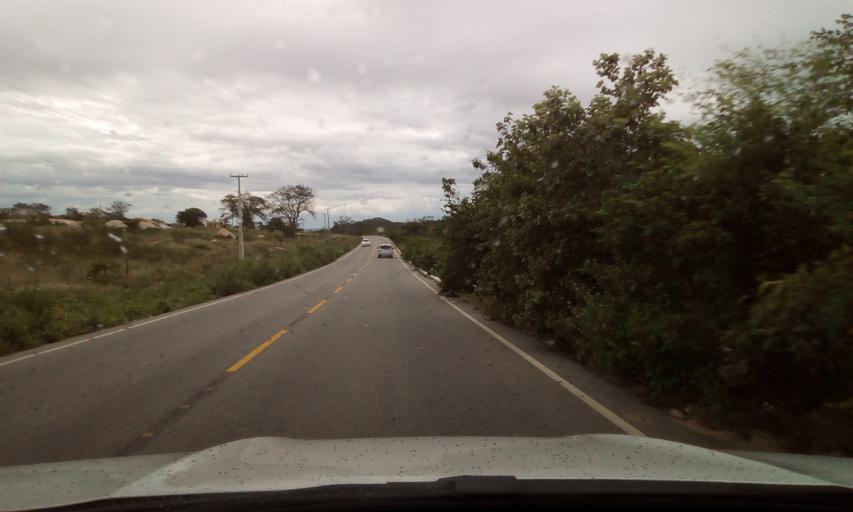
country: BR
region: Paraiba
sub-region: Picui
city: Picui
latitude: -6.5672
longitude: -36.2758
